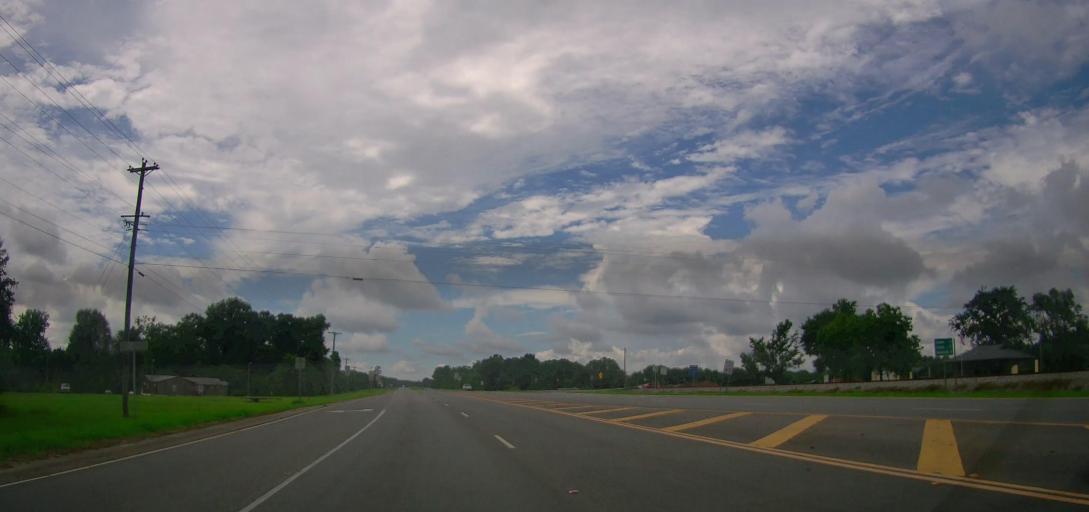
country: US
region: Georgia
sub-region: Dodge County
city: Eastman
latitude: 32.1066
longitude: -83.0750
